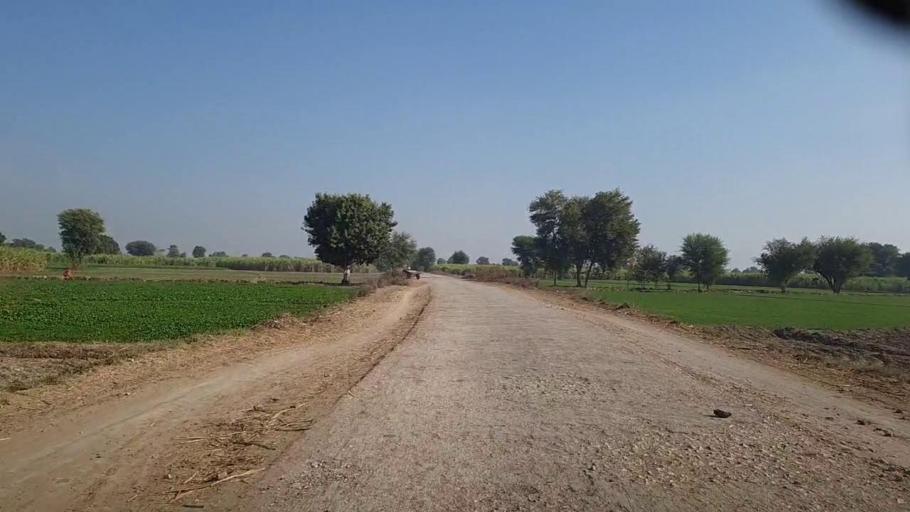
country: PK
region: Sindh
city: Darya Khan Marri
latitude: 26.6704
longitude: 68.3285
